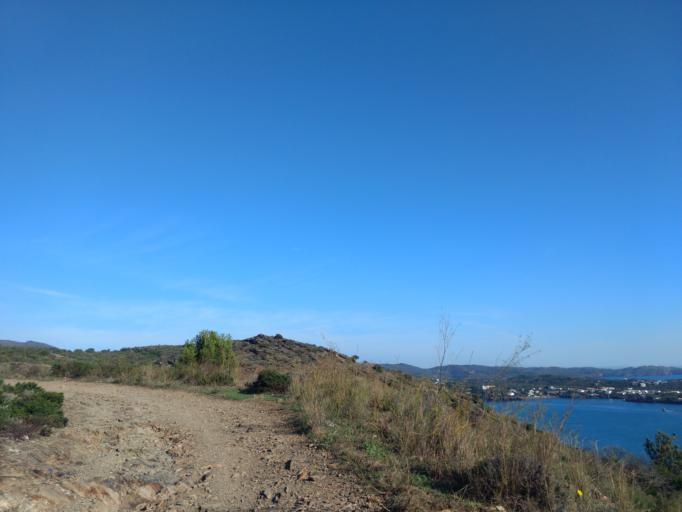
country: ES
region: Catalonia
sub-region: Provincia de Girona
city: Cadaques
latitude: 42.2730
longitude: 3.2791
